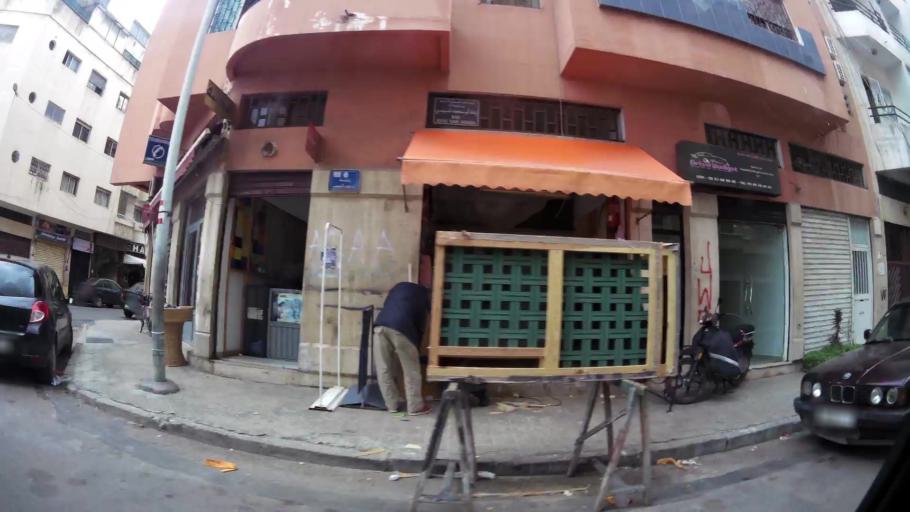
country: MA
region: Grand Casablanca
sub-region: Casablanca
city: Casablanca
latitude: 33.5970
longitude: -7.6448
